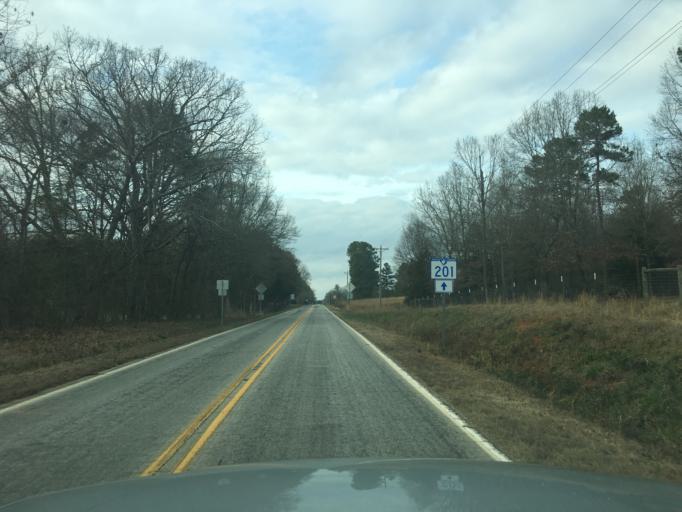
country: US
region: South Carolina
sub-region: Abbeville County
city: Due West
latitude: 34.3000
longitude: -82.4521
